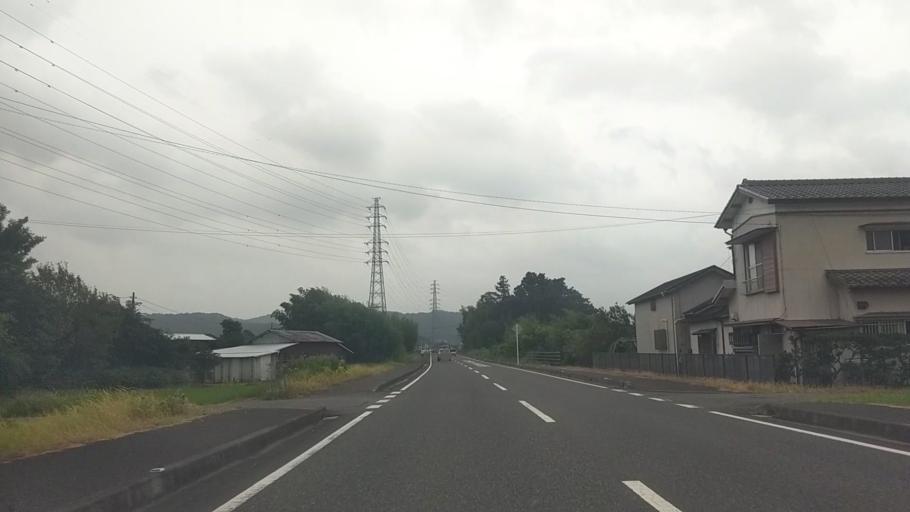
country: JP
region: Chiba
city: Kisarazu
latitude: 35.3129
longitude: 140.0578
